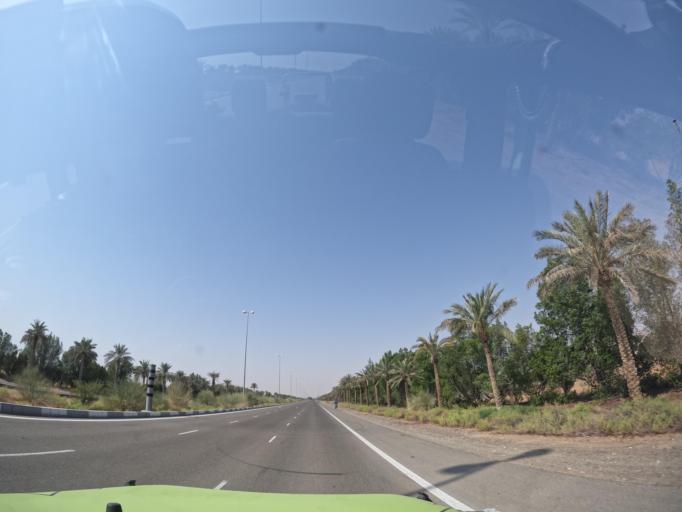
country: AE
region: Abu Dhabi
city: Al Ain
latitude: 24.2106
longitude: 55.6052
